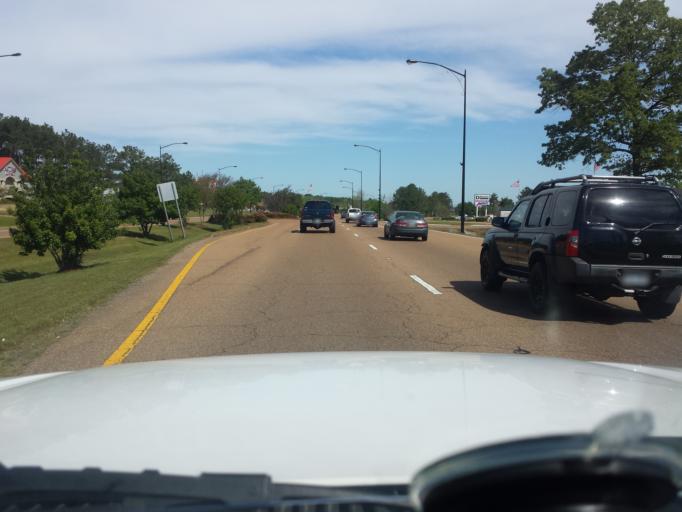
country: US
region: Mississippi
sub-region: Rankin County
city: Pearl
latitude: 32.2772
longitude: -90.0726
